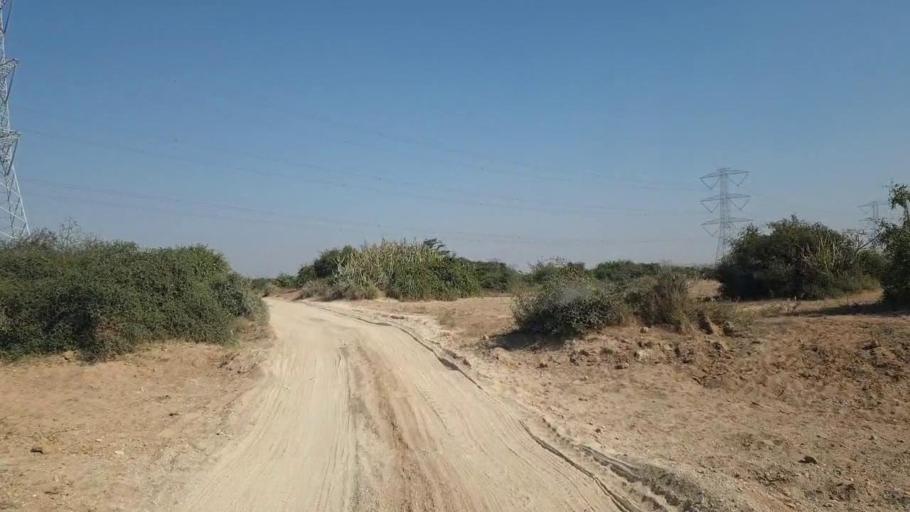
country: PK
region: Sindh
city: Gharo
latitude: 25.1959
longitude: 67.7422
